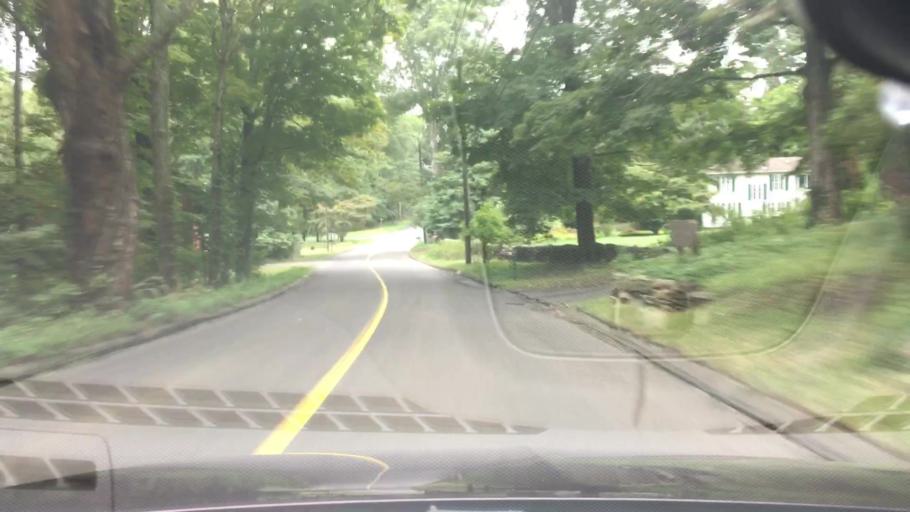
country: US
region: Connecticut
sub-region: New Haven County
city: Madison
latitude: 41.3322
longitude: -72.5861
